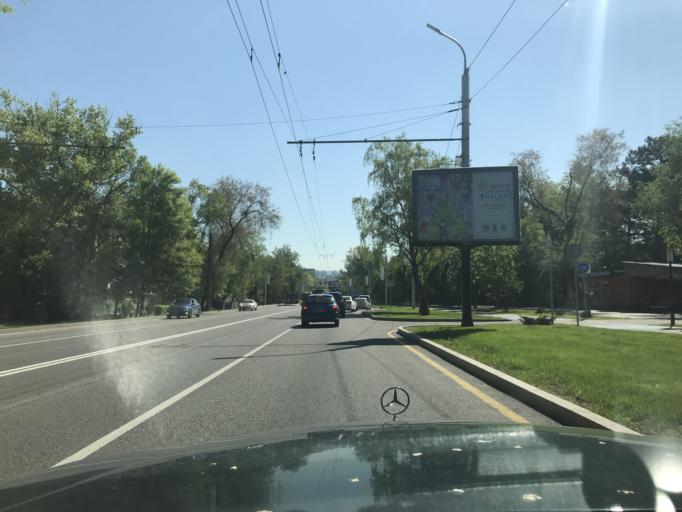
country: KZ
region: Almaty Qalasy
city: Almaty
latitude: 43.2263
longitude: 76.9129
